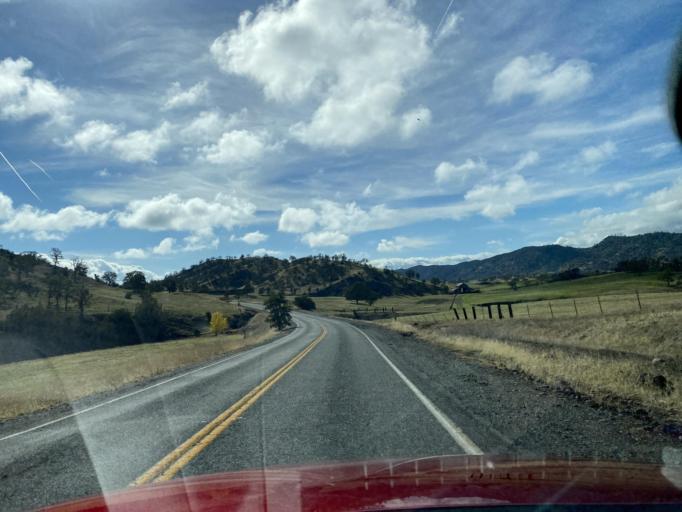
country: US
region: California
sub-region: Glenn County
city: Willows
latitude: 39.5050
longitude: -122.5259
